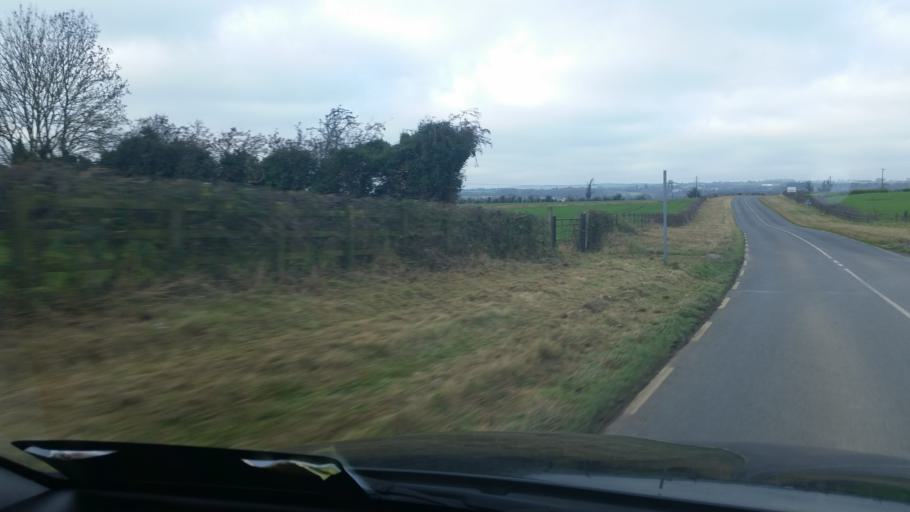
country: IE
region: Leinster
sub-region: Lu
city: Tullyallen
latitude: 53.7092
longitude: -6.4107
